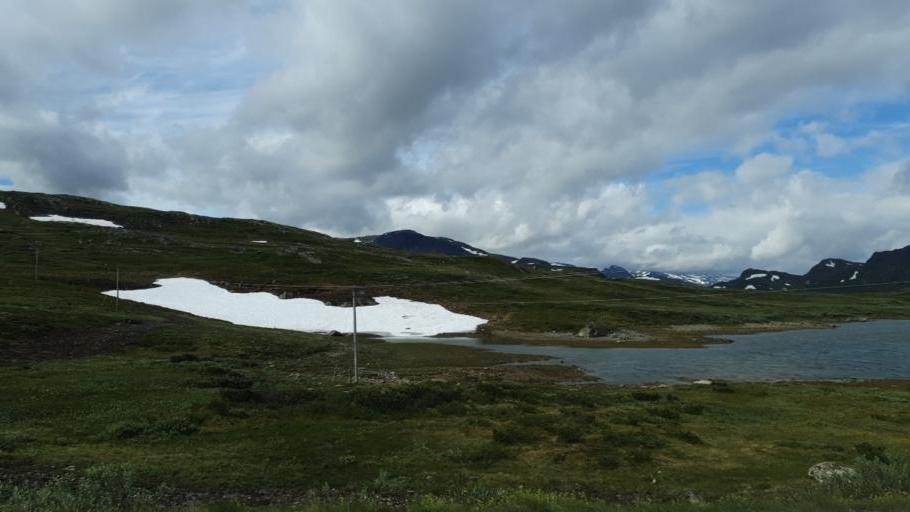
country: NO
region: Oppland
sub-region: Vestre Slidre
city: Slidre
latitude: 61.3269
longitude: 8.8012
